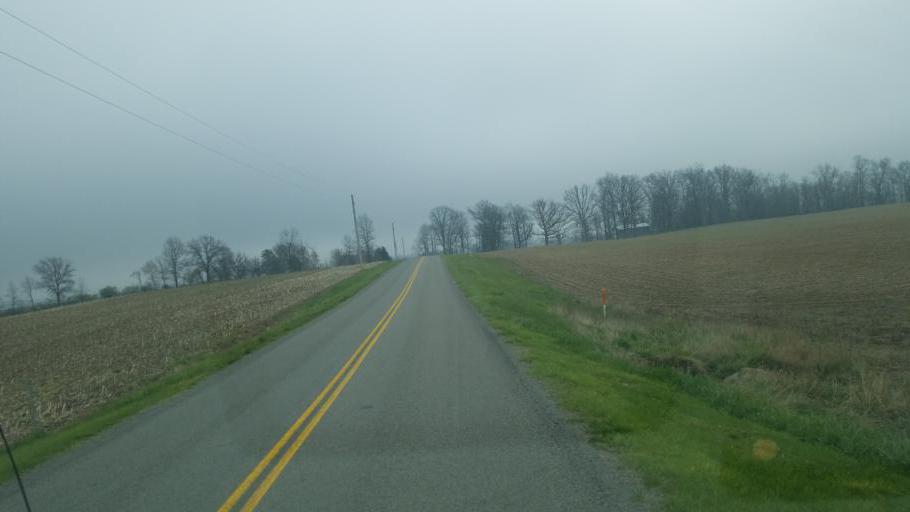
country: US
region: Ohio
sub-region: Logan County
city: Bellefontaine
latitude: 40.4045
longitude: -83.8197
